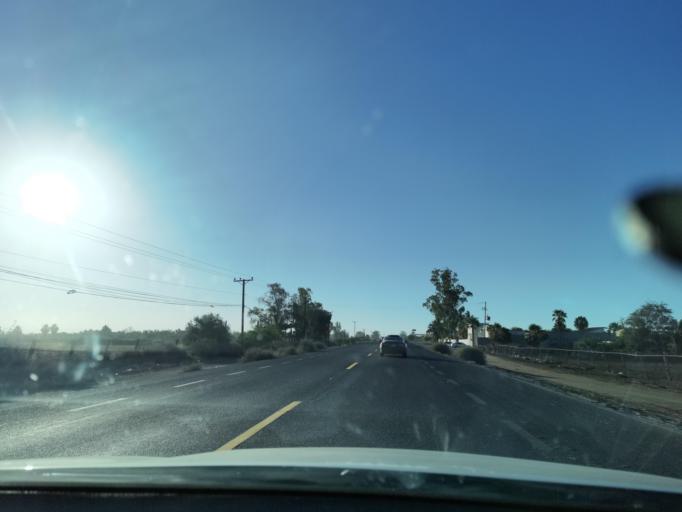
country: MX
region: Baja California
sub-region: Mexicali
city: Islas Agrarias Grupo A
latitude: 32.6467
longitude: -115.3252
